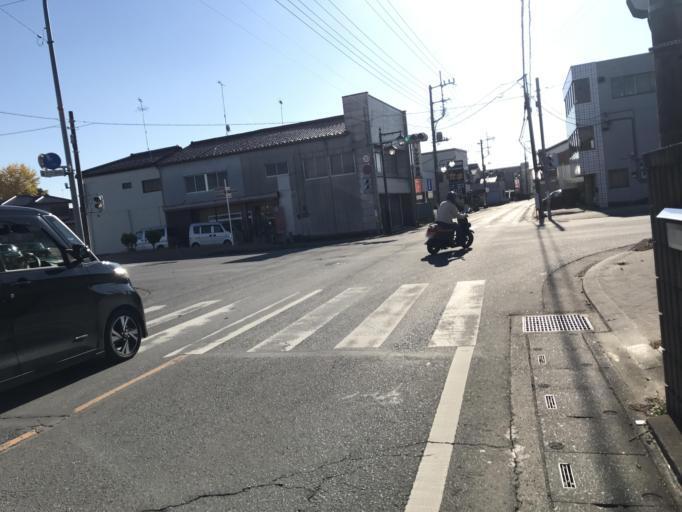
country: JP
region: Ibaraki
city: Sakai
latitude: 36.1140
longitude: 139.7966
